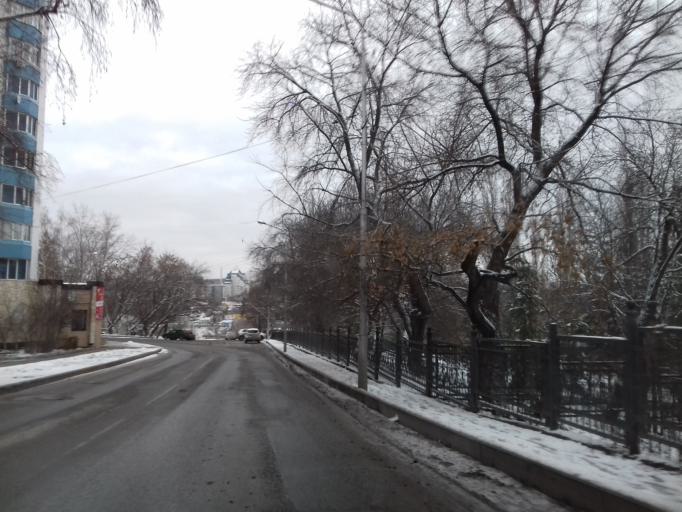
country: RU
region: Bashkortostan
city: Ufa
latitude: 54.7128
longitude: 55.9535
